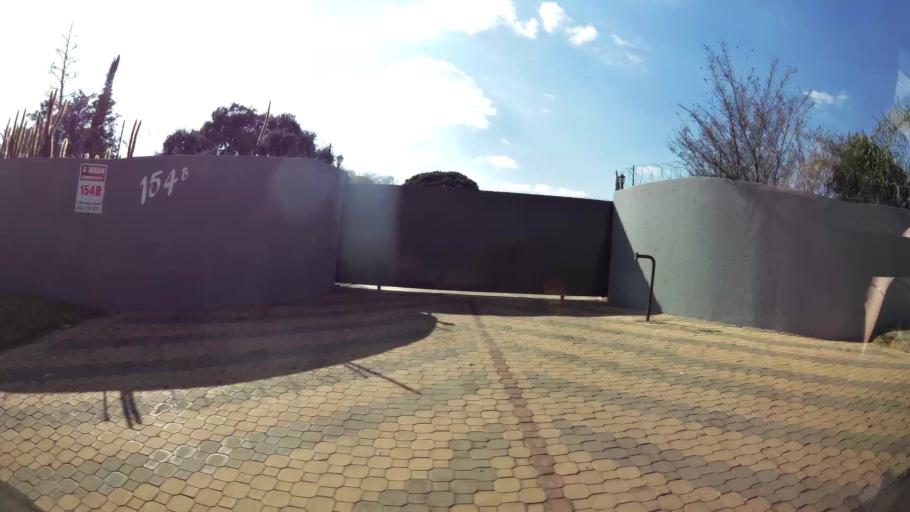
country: ZA
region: Gauteng
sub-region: Ekurhuleni Metropolitan Municipality
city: Benoni
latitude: -26.0899
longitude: 28.3304
